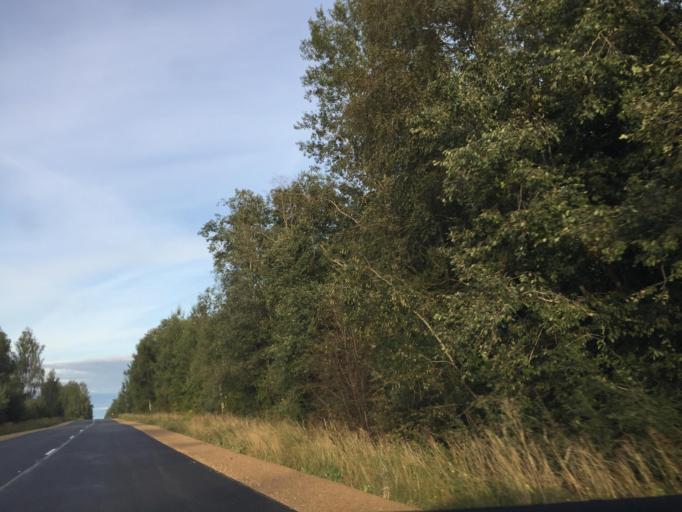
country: LV
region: Viesite
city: Viesite
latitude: 56.3504
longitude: 25.5891
